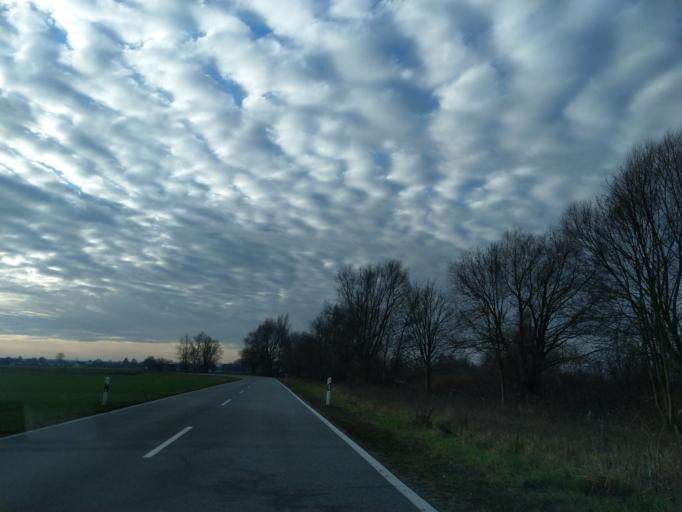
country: DE
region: Bavaria
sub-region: Lower Bavaria
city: Aholming
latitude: 48.7544
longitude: 12.9050
